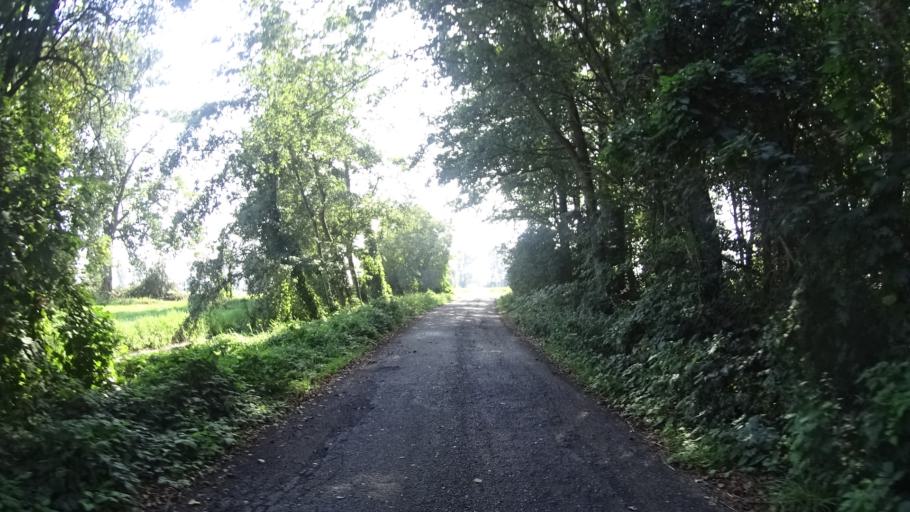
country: DE
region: Brandenburg
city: Neu Zauche
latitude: 51.9038
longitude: 14.0802
